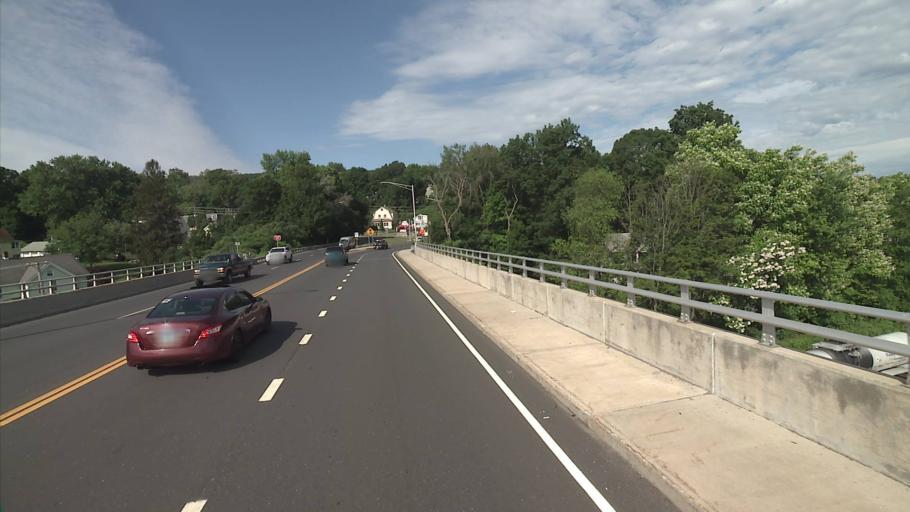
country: US
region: Connecticut
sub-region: New Haven County
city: Naugatuck
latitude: 41.4844
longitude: -73.0544
